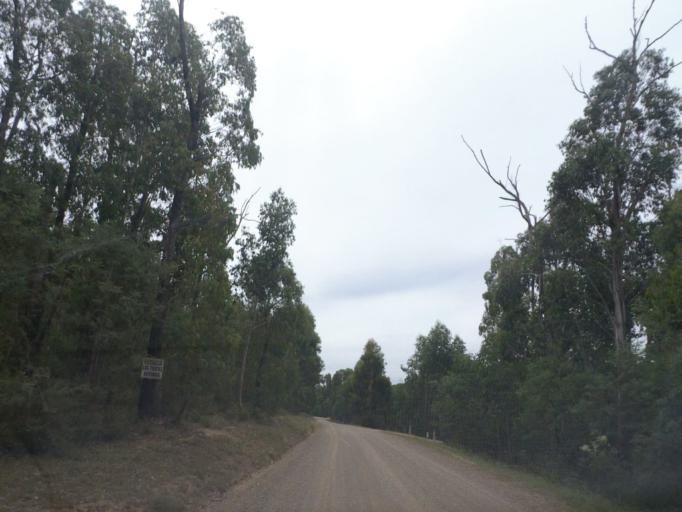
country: AU
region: Victoria
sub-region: Yarra Ranges
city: Healesville
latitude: -37.4273
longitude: 145.5690
